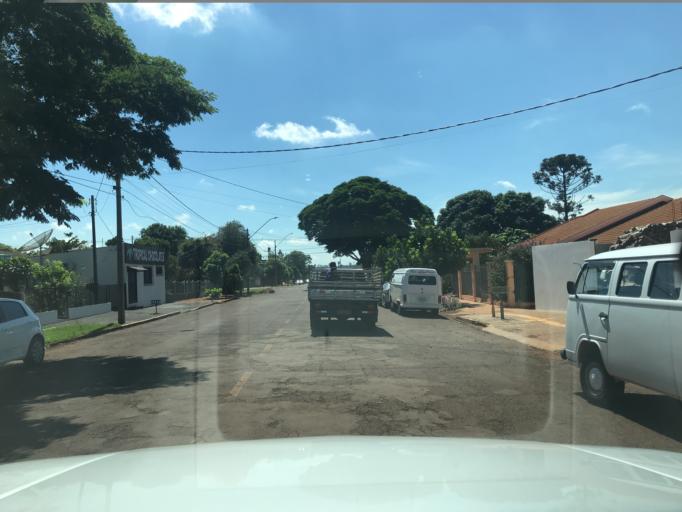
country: BR
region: Parana
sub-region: Palotina
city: Palotina
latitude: -24.2841
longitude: -53.8346
